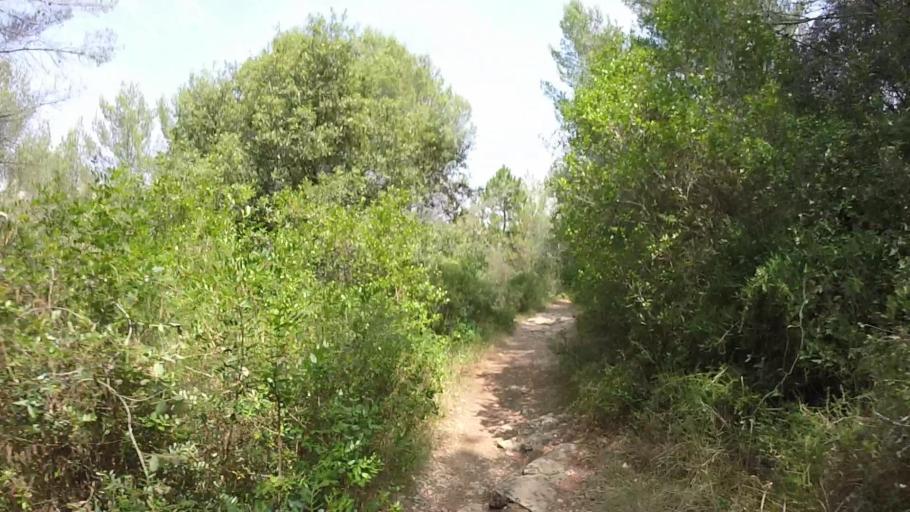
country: FR
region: Provence-Alpes-Cote d'Azur
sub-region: Departement des Alpes-Maritimes
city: Valbonne
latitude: 43.6307
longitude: 7.0414
